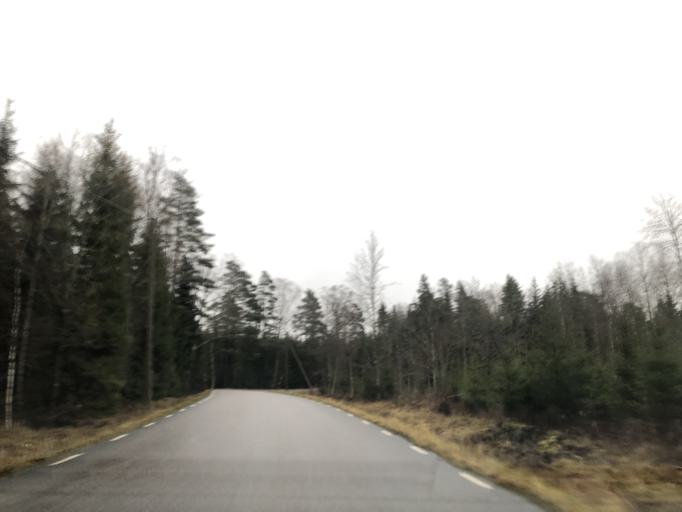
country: SE
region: Vaestra Goetaland
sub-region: Ulricehamns Kommun
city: Ulricehamn
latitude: 57.8520
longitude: 13.2538
